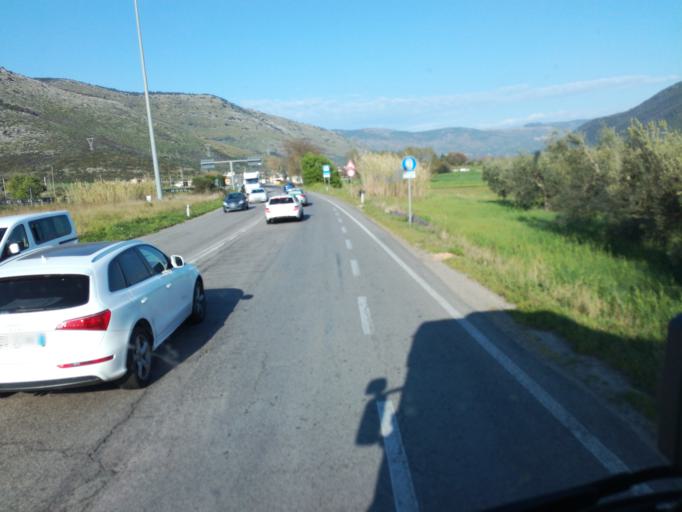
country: IT
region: Latium
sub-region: Provincia di Latina
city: Roccasecca dei Volsci
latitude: 41.4958
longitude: 13.2121
